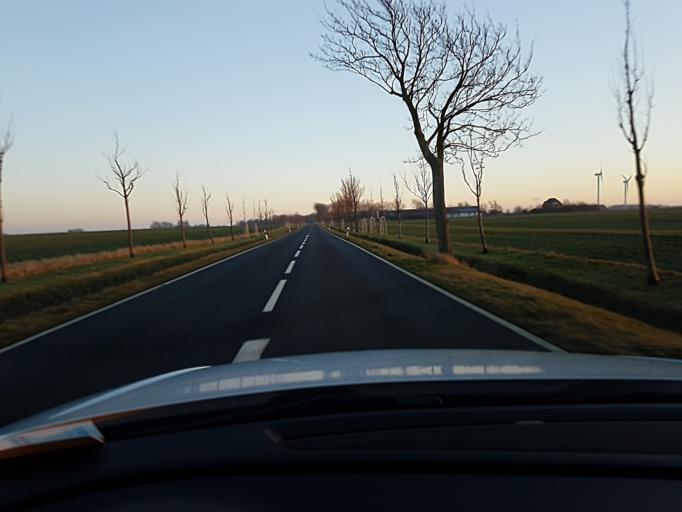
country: DE
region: Mecklenburg-Vorpommern
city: Wiek
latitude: 54.6069
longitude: 13.2831
